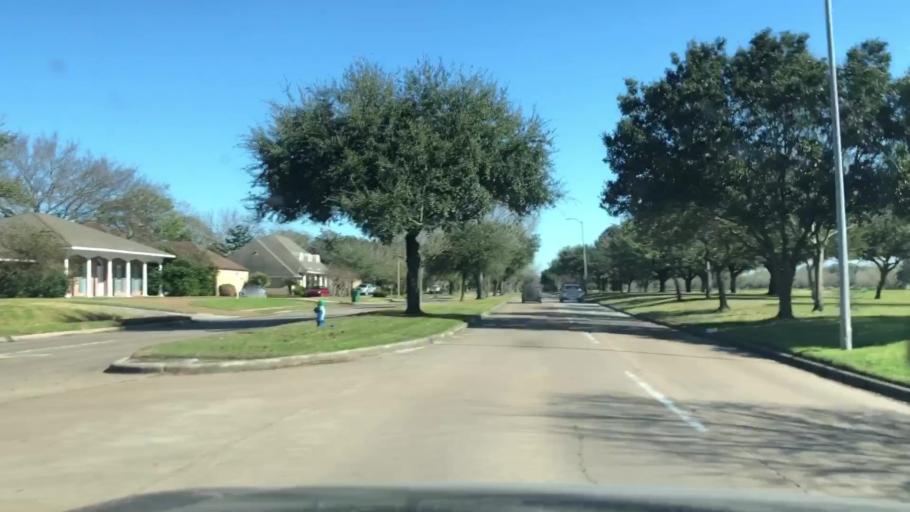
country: US
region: Texas
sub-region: Harris County
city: Bellaire
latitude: 29.6785
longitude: -95.4738
